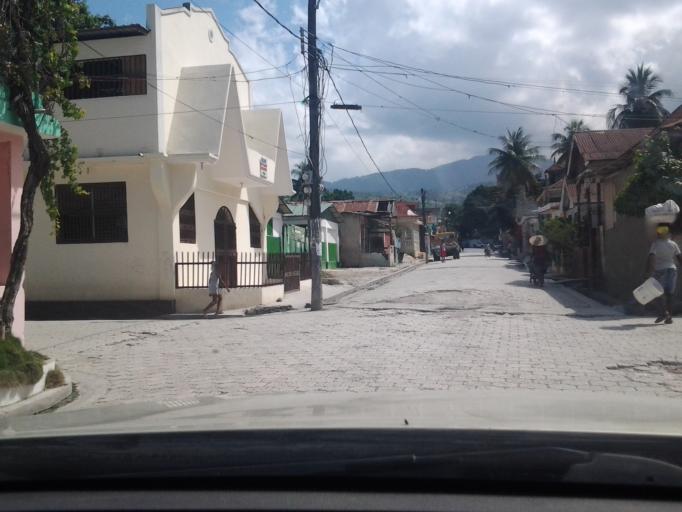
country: HT
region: Ouest
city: Tigwav
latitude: 18.4317
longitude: -72.8650
